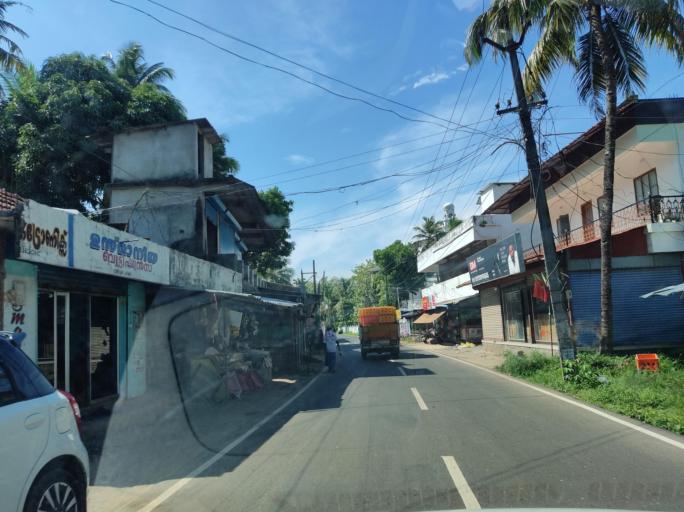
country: IN
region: Kerala
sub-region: Alappuzha
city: Kayankulam
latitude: 9.2786
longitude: 76.3998
